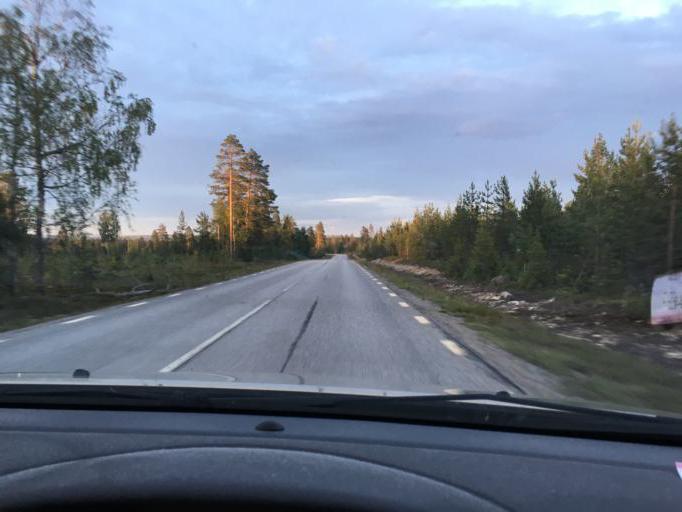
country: SE
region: Norrbotten
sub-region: Kalix Kommun
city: Toere
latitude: 66.0539
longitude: 22.4670
